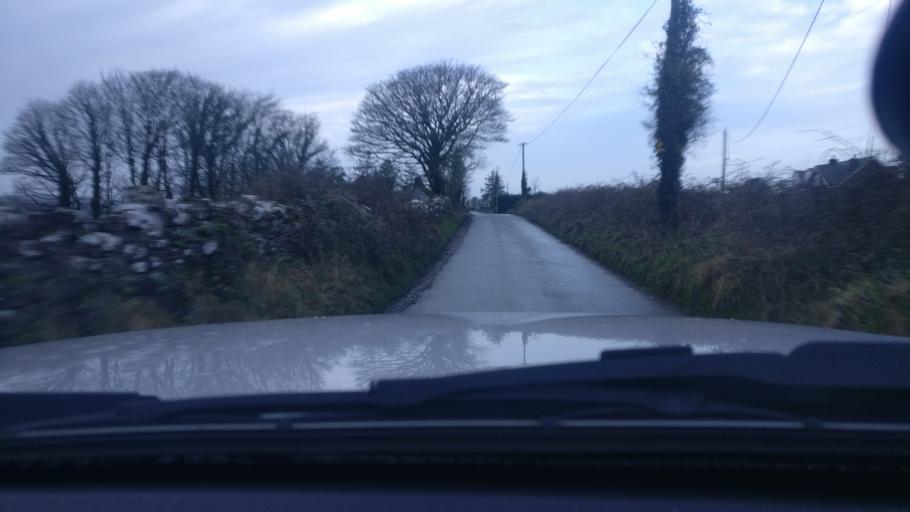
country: IE
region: Connaught
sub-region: County Galway
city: Loughrea
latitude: 53.1640
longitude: -8.5383
